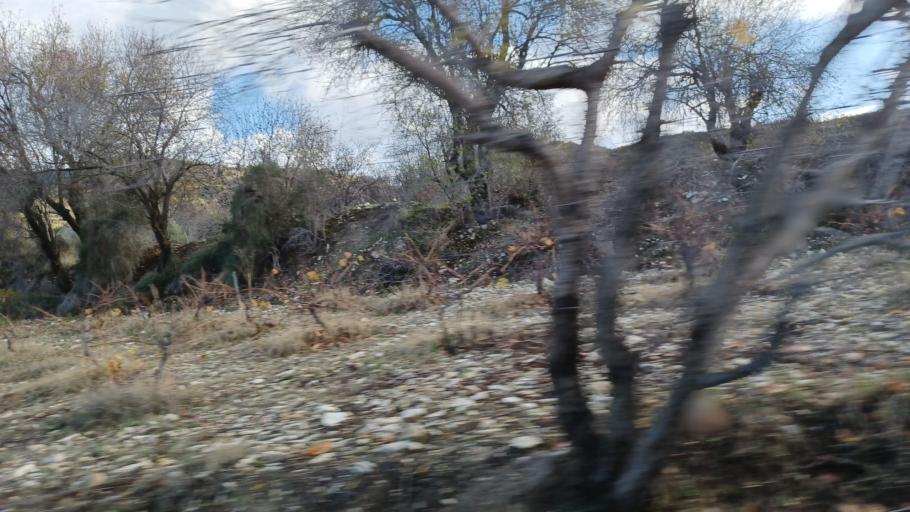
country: CY
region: Limassol
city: Pachna
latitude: 34.8599
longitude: 32.6915
